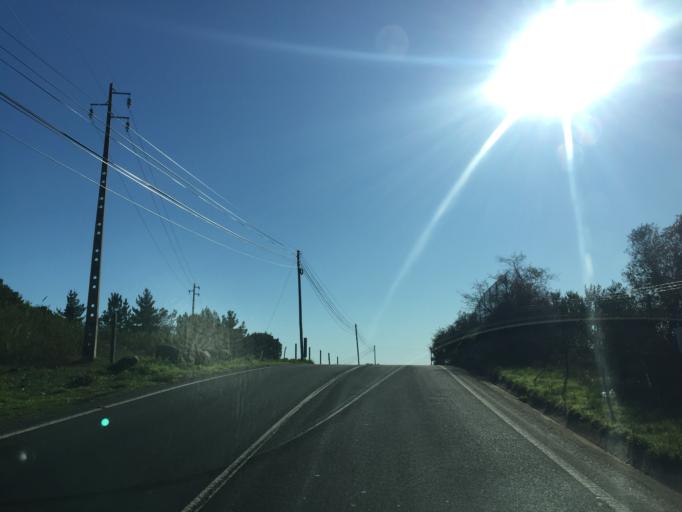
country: PT
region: Lisbon
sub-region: Sintra
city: Belas
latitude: 38.8043
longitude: -9.2865
